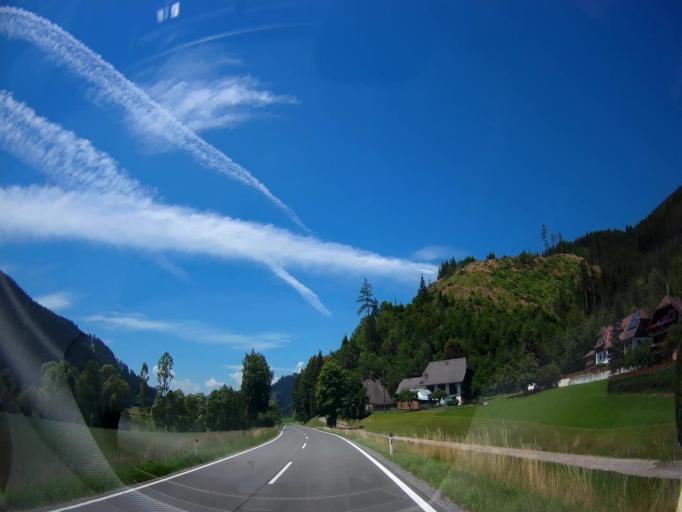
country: AT
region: Carinthia
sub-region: Politischer Bezirk Sankt Veit an der Glan
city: Micheldorf
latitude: 46.9001
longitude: 14.4240
